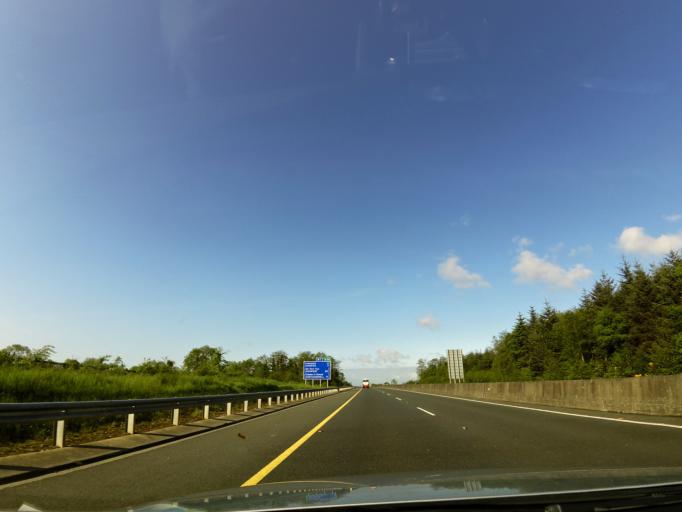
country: IE
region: Munster
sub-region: North Tipperary
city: Newport
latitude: 52.7515
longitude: -8.4222
